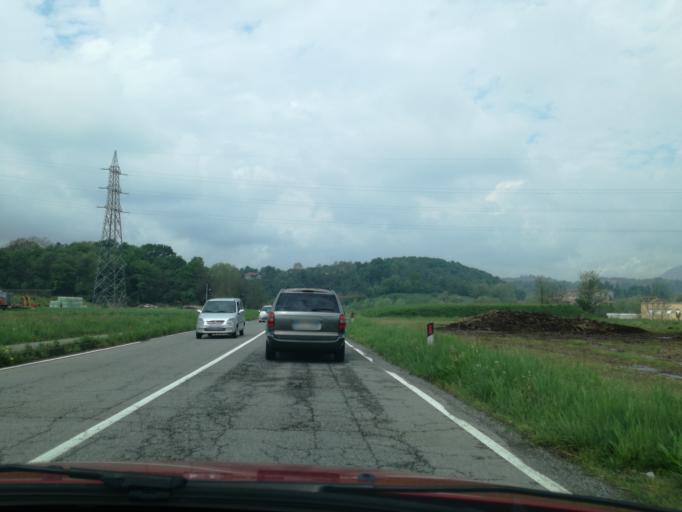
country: IT
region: Lombardy
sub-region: Provincia di Lecco
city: Canova-San Zeno
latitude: 45.7127
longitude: 9.4017
